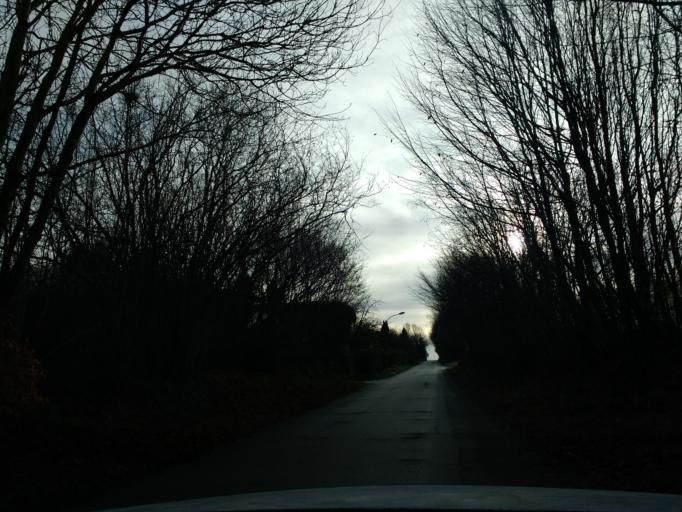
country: DE
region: Schleswig-Holstein
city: Nindorf
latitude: 54.1314
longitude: 9.6934
